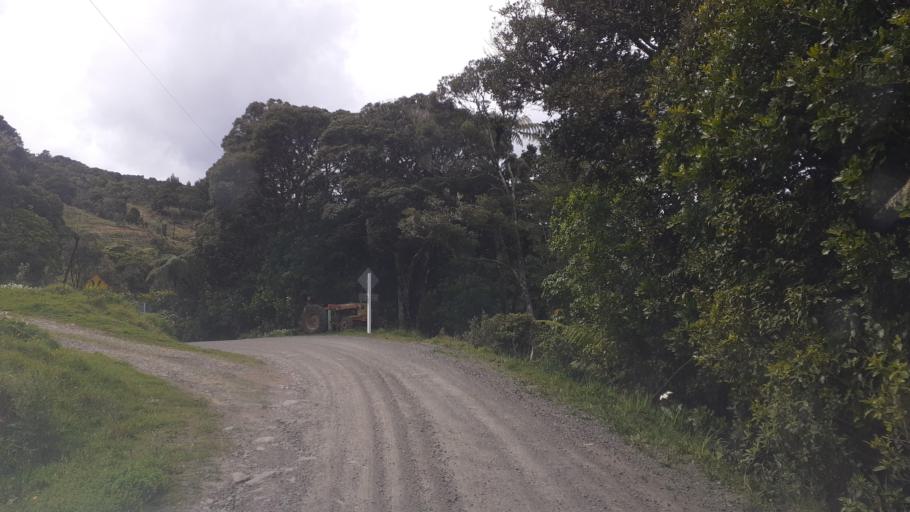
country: NZ
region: Northland
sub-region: Far North District
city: Waimate North
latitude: -35.5736
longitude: 173.5669
